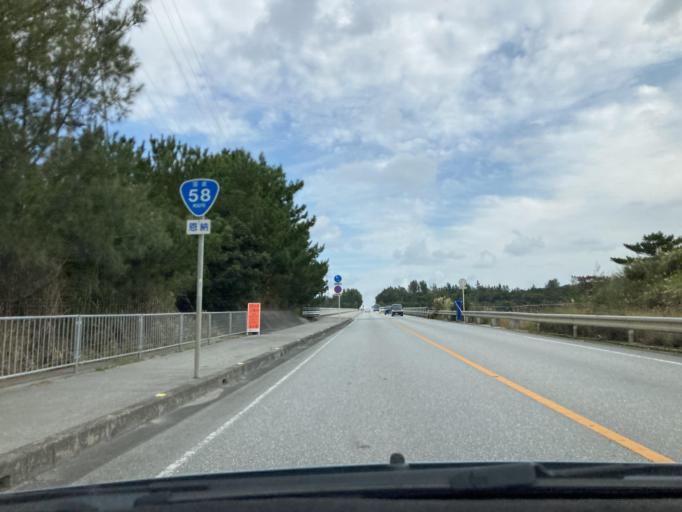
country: JP
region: Okinawa
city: Ishikawa
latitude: 26.4941
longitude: 127.8568
